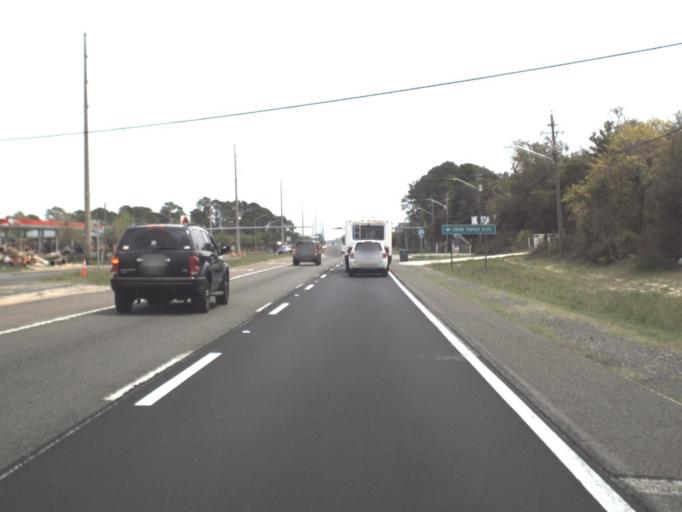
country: US
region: Florida
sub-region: Santa Rosa County
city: Navarre
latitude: 30.4095
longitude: -86.8139
